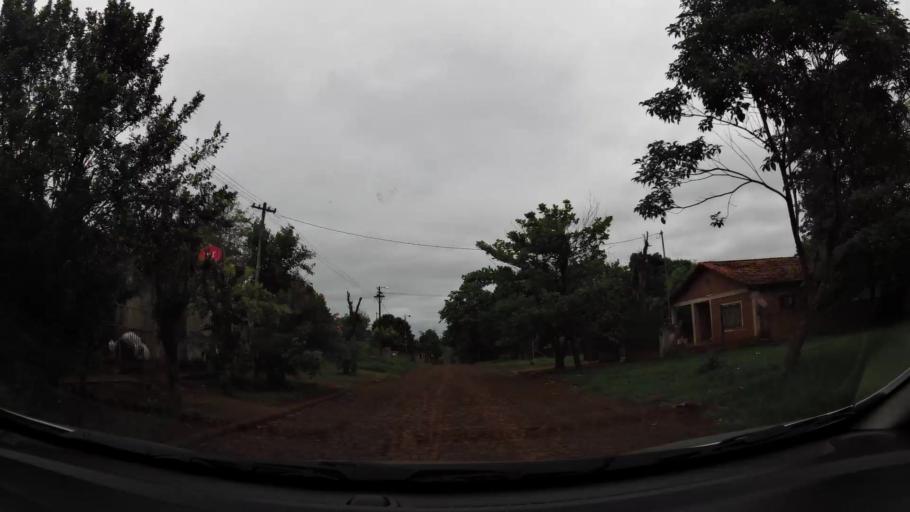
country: PY
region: Alto Parana
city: Presidente Franco
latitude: -25.4876
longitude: -54.7968
